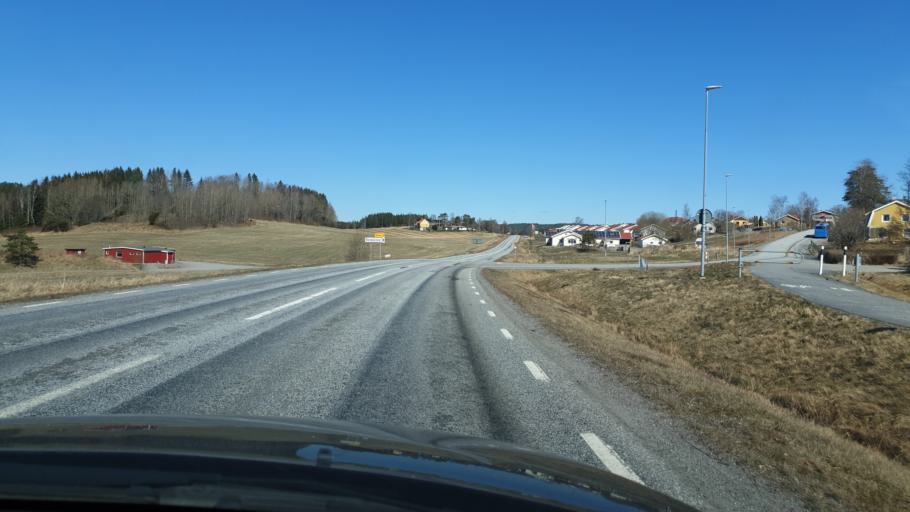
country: SE
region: Vaestra Goetaland
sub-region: Tanums Kommun
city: Tanumshede
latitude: 58.7704
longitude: 11.5567
